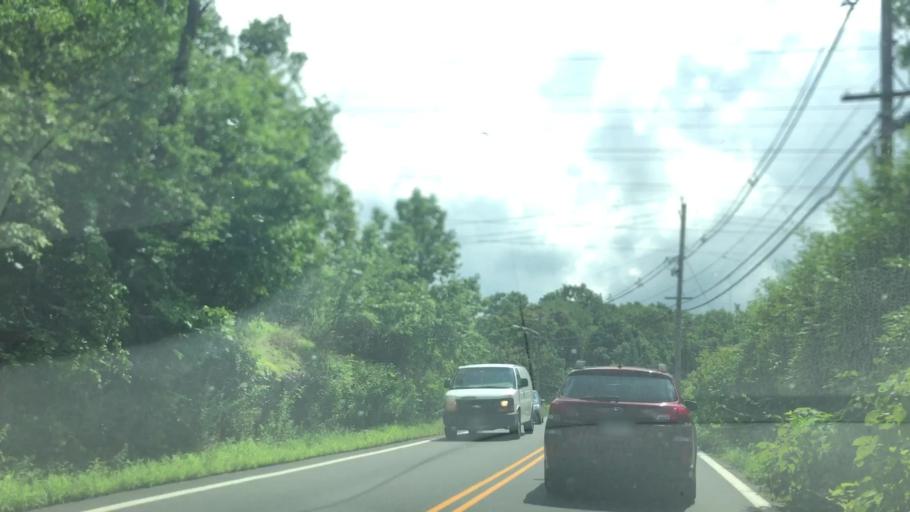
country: US
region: New Jersey
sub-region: Passaic County
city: Little Falls
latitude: 40.8653
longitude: -74.2031
